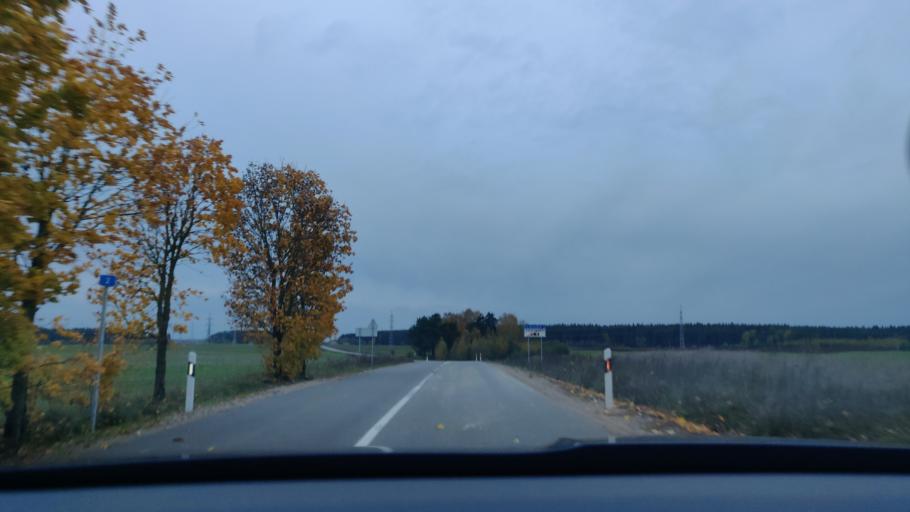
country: LT
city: Lentvaris
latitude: 54.5922
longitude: 25.0468
